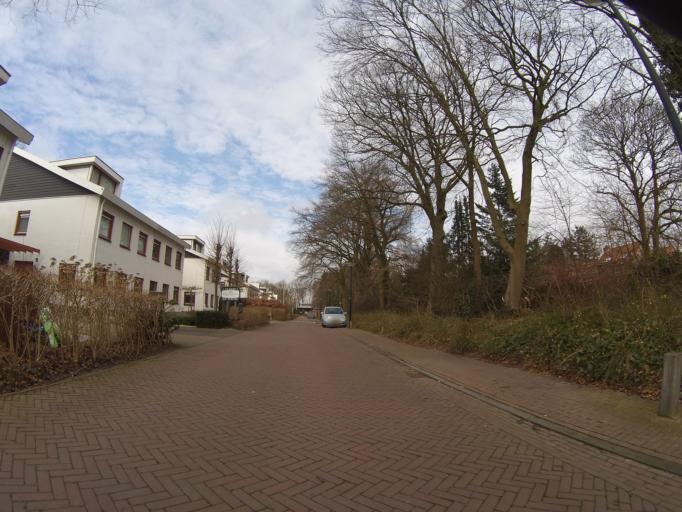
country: NL
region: Utrecht
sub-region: Gemeente Amersfoort
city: Amersfoort
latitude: 52.1433
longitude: 5.3622
